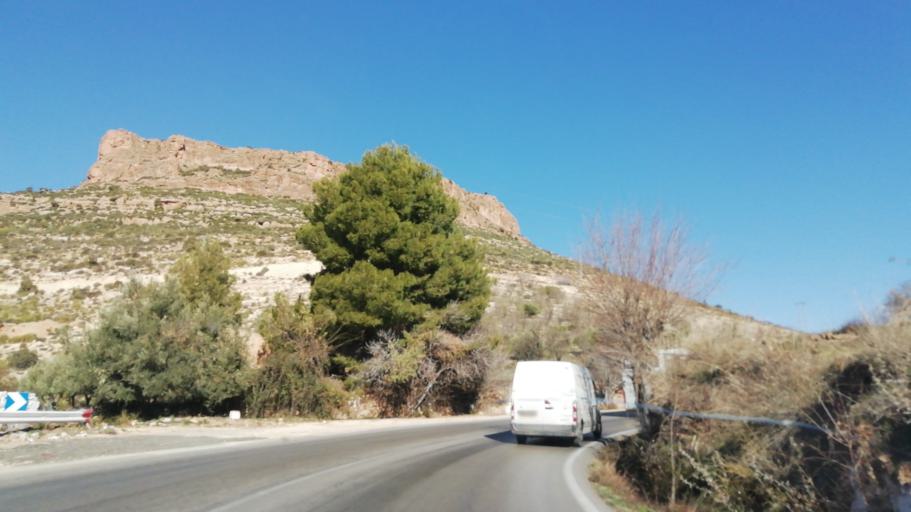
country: DZ
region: Tlemcen
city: Sebdou
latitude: 34.6866
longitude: -1.3184
